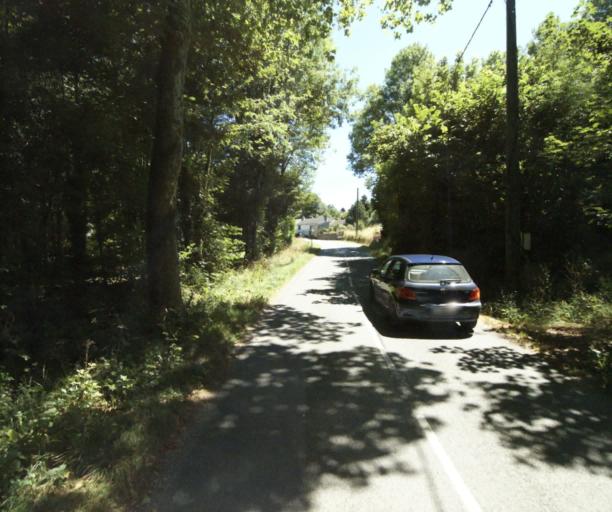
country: FR
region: Midi-Pyrenees
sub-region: Departement du Tarn
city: Dourgne
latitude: 43.4315
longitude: 2.1640
